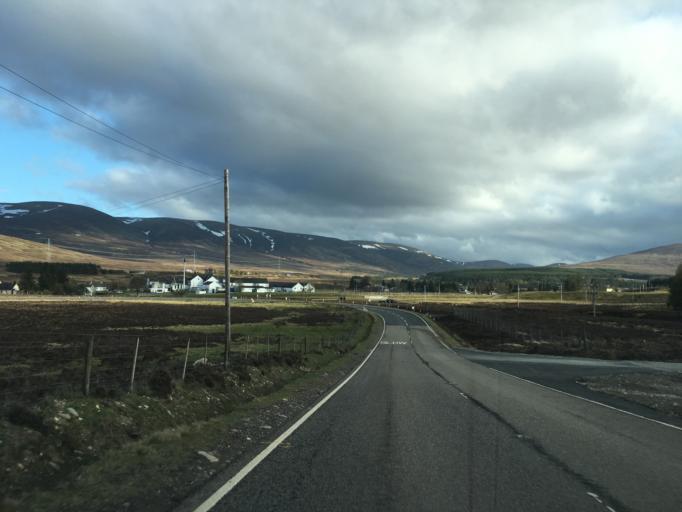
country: GB
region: Scotland
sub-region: Highland
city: Kingussie
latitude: 56.9442
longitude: -4.2428
